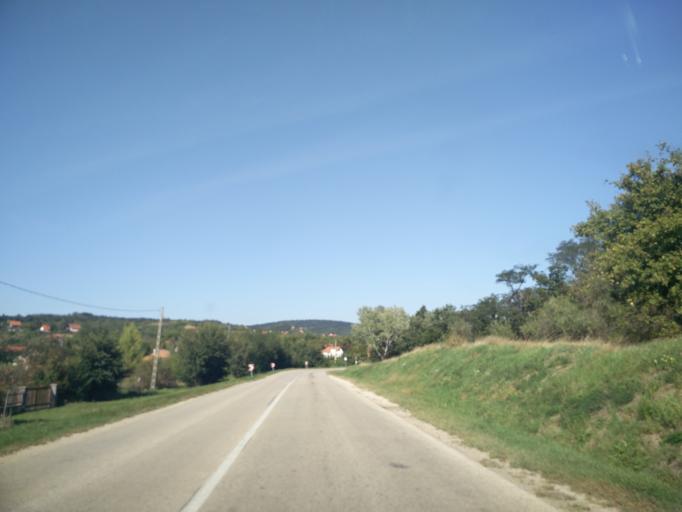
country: HU
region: Fejer
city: Pakozd
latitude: 47.2347
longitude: 18.5811
